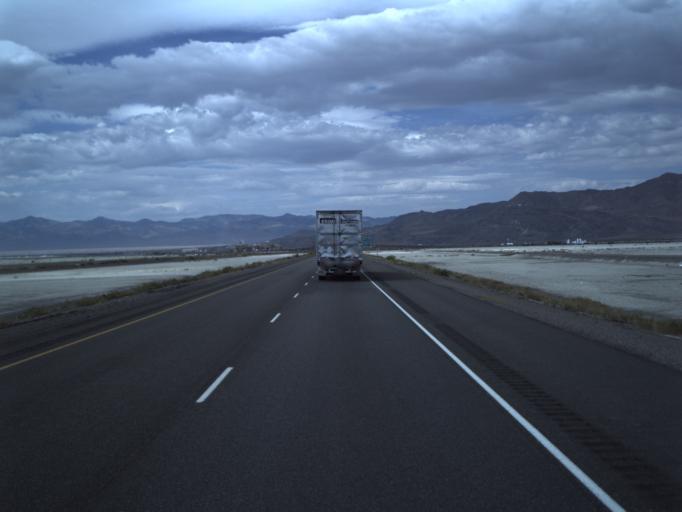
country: US
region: Utah
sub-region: Tooele County
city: Wendover
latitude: 40.7413
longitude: -113.9485
